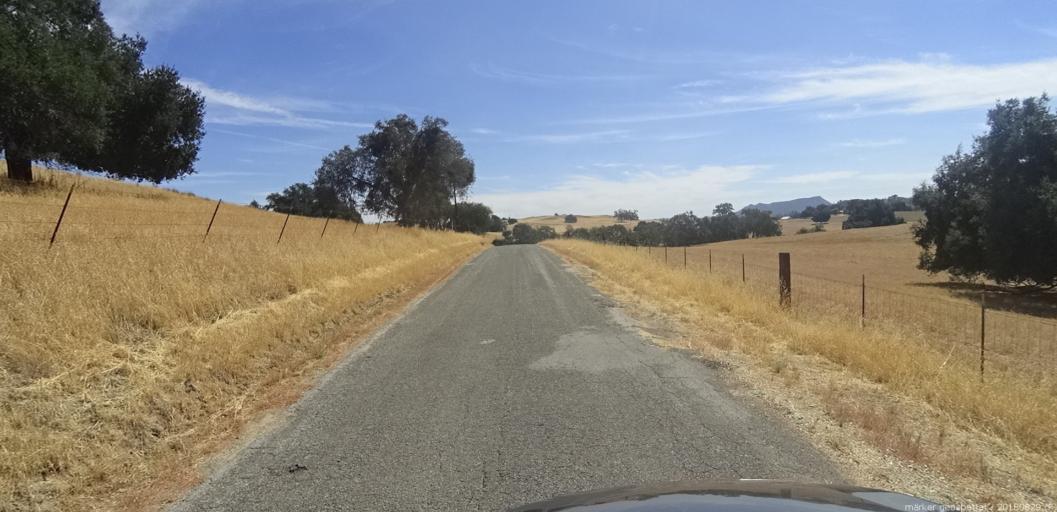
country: US
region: California
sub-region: San Luis Obispo County
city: Lake Nacimiento
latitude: 35.8076
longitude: -121.0564
